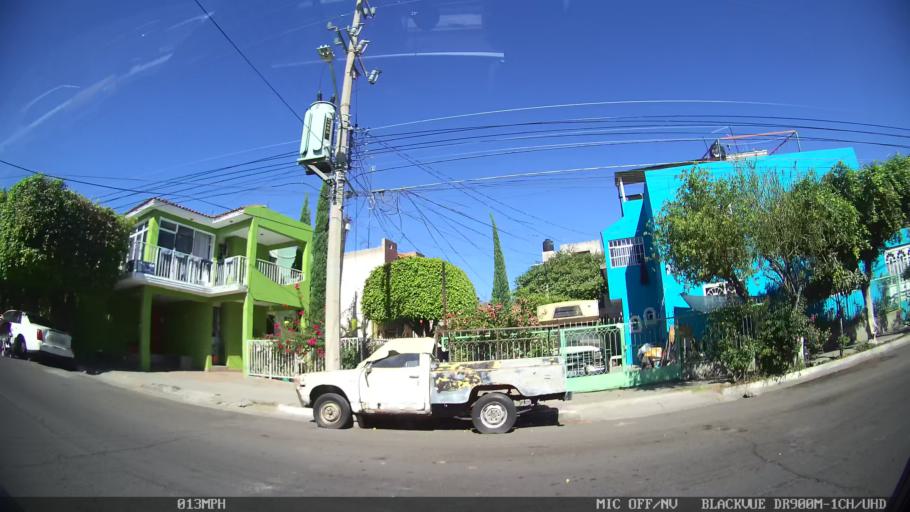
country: MX
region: Jalisco
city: Tlaquepaque
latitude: 20.6802
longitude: -103.2751
